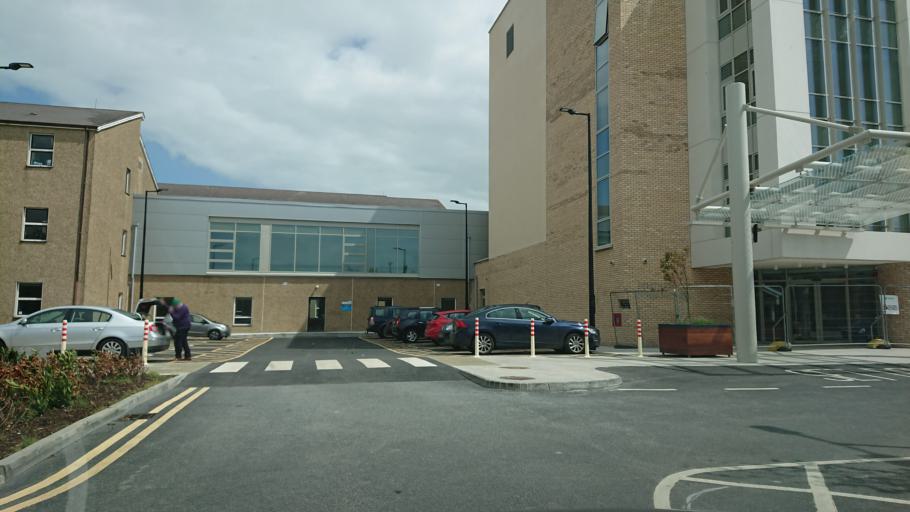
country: IE
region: Munster
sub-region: Waterford
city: Waterford
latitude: 52.2481
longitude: -7.0786
